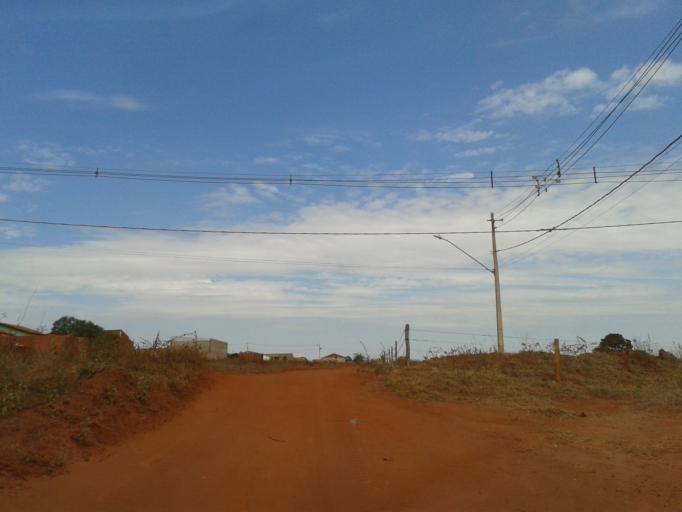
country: BR
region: Minas Gerais
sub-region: Santa Vitoria
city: Santa Vitoria
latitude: -18.8522
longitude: -50.1374
